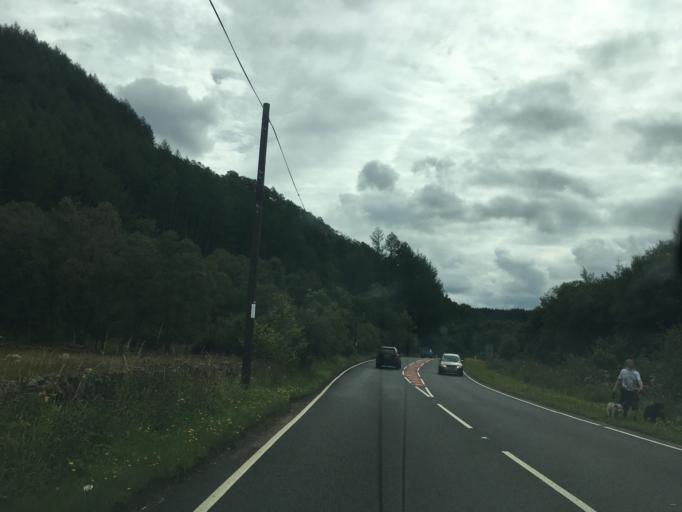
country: GB
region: Scotland
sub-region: Stirling
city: Callander
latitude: 56.2556
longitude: -4.2820
